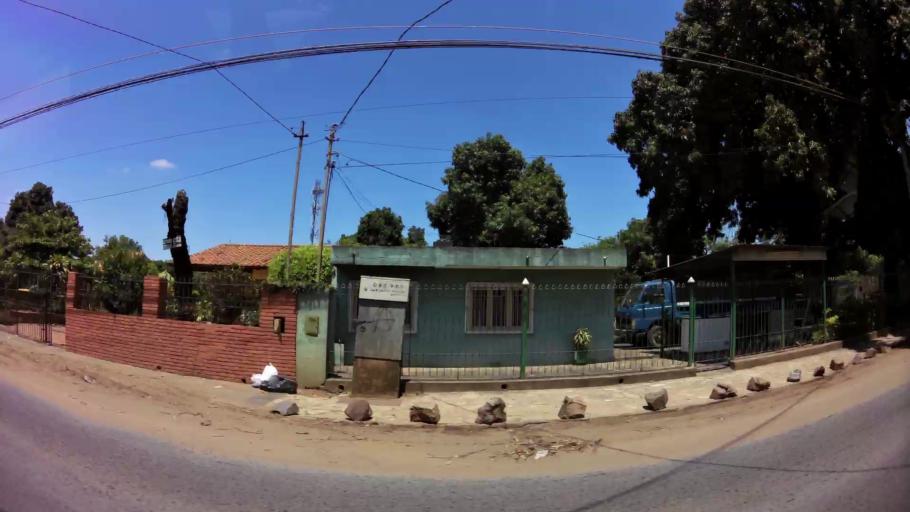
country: PY
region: Central
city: Nemby
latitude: -25.3954
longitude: -57.5416
